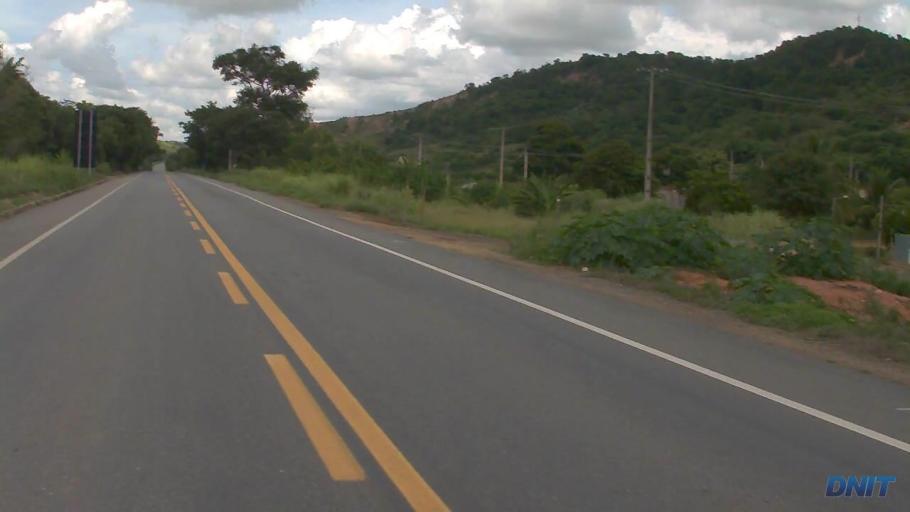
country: BR
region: Minas Gerais
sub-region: Governador Valadares
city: Governador Valadares
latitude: -18.9474
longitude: -42.0683
